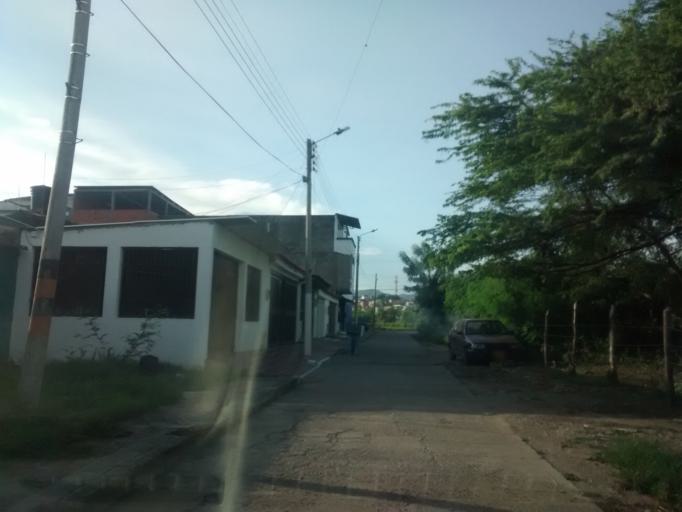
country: CO
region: Cundinamarca
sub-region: Girardot
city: Girardot City
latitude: 4.3087
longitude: -74.7927
